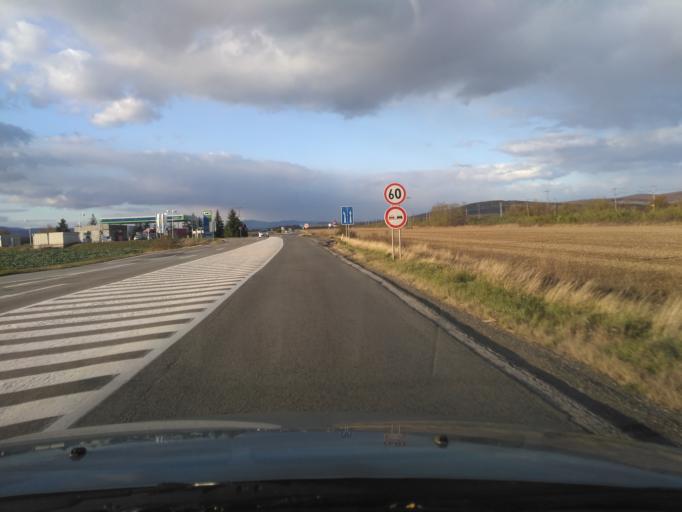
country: HU
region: Borsod-Abauj-Zemplen
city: Satoraljaujhely
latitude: 48.4268
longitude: 21.6603
